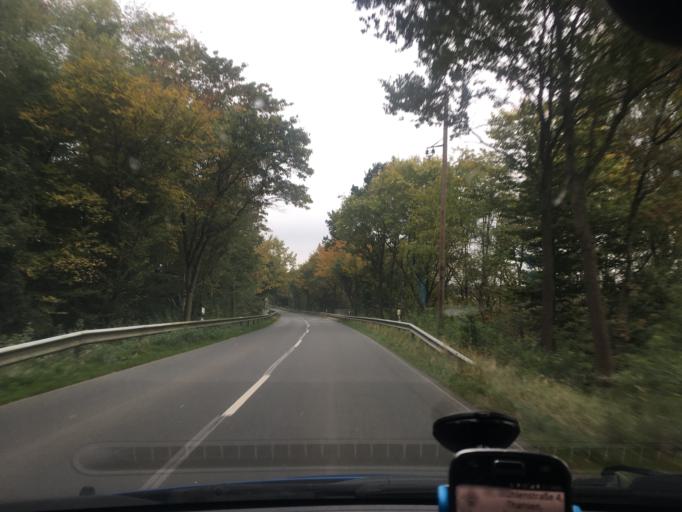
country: DE
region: Lower Saxony
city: Soderstorf
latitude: 53.1290
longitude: 10.1768
